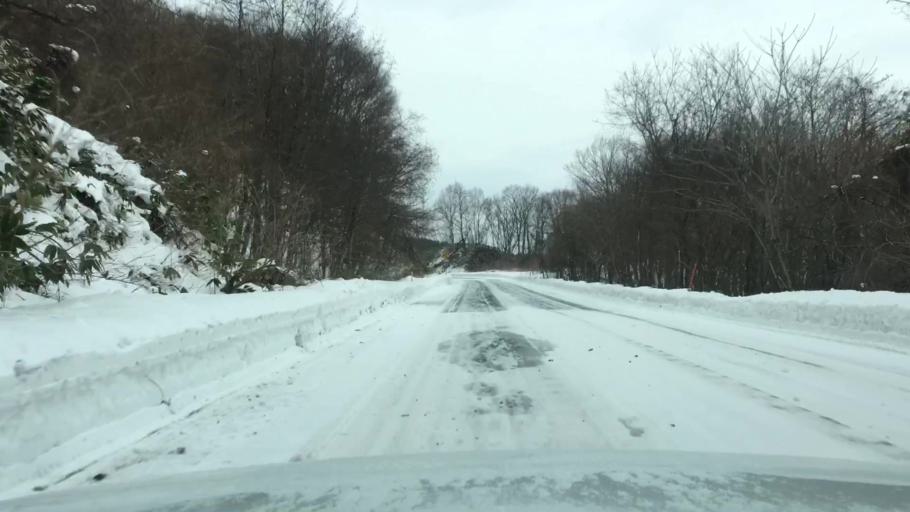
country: JP
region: Iwate
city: Shizukuishi
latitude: 39.9414
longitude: 140.9966
